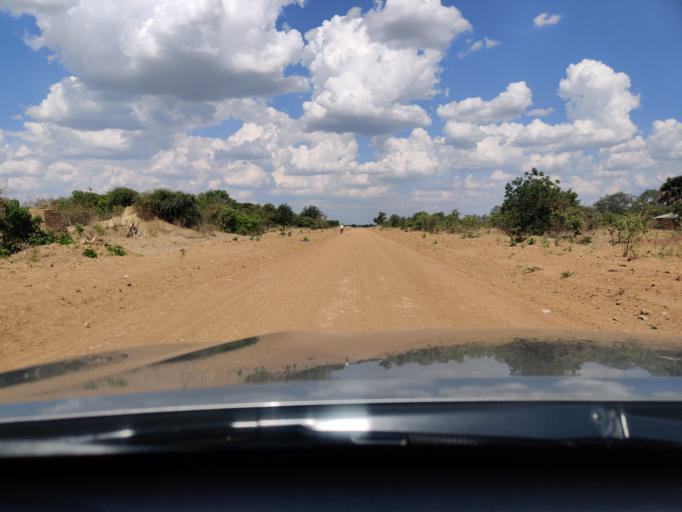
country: ZM
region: Central
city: Chibombo
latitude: -14.7592
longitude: 27.8725
